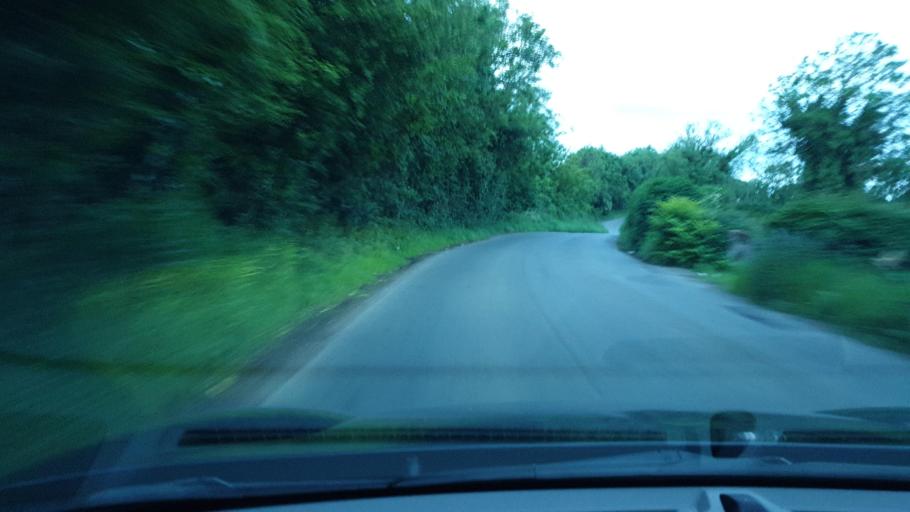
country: IE
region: Leinster
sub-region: An Mhi
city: Ashbourne
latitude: 53.5682
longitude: -6.4032
